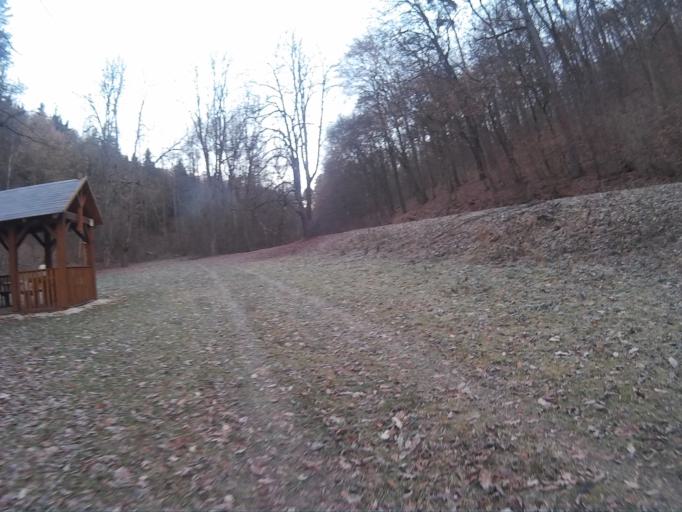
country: HU
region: Borsod-Abauj-Zemplen
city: Putnok
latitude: 48.3322
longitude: 20.4345
